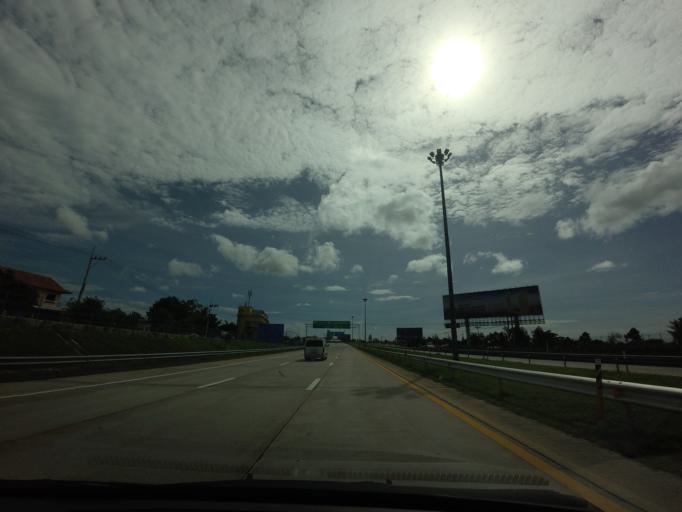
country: TH
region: Chon Buri
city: Phatthaya
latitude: 12.9506
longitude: 100.9439
